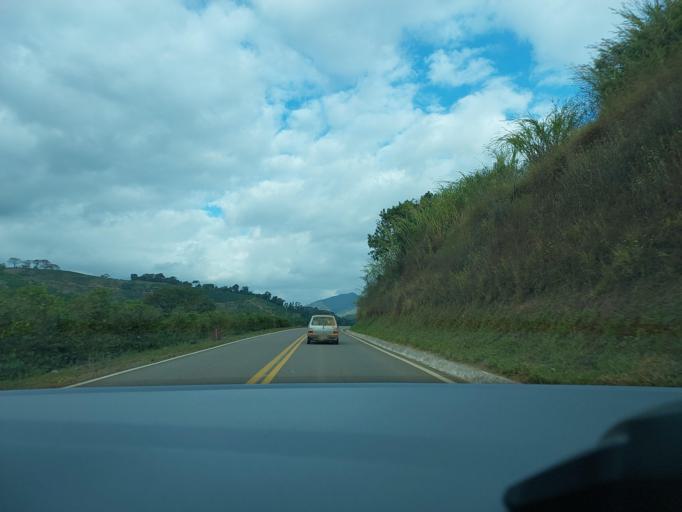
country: BR
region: Minas Gerais
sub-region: Visconde Do Rio Branco
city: Visconde do Rio Branco
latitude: -20.9303
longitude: -42.6340
